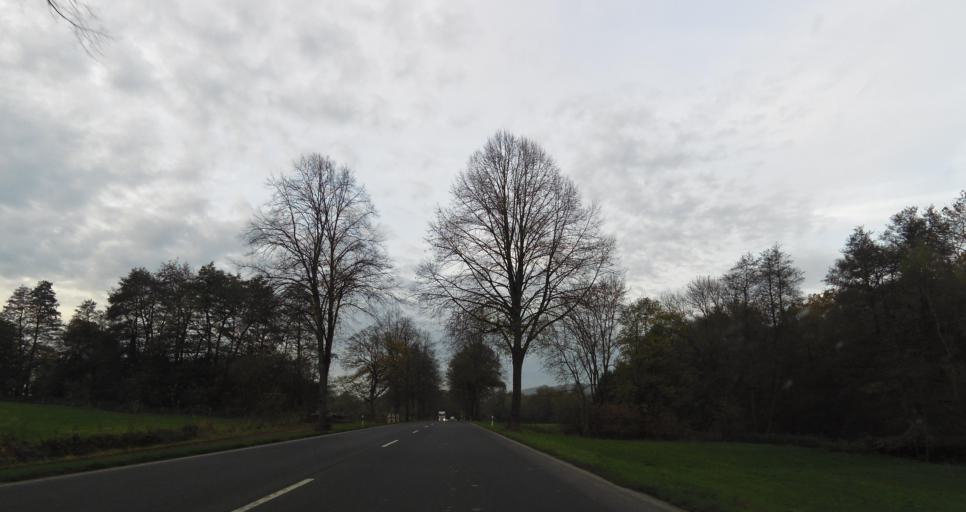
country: DE
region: Lower Saxony
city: Holzen
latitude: 51.9138
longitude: 9.6671
